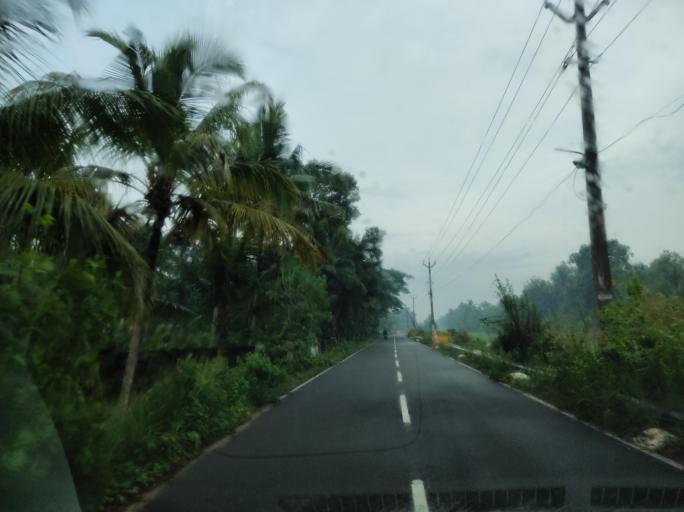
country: IN
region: Kerala
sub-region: Alappuzha
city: Alleppey
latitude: 9.5860
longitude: 76.3325
